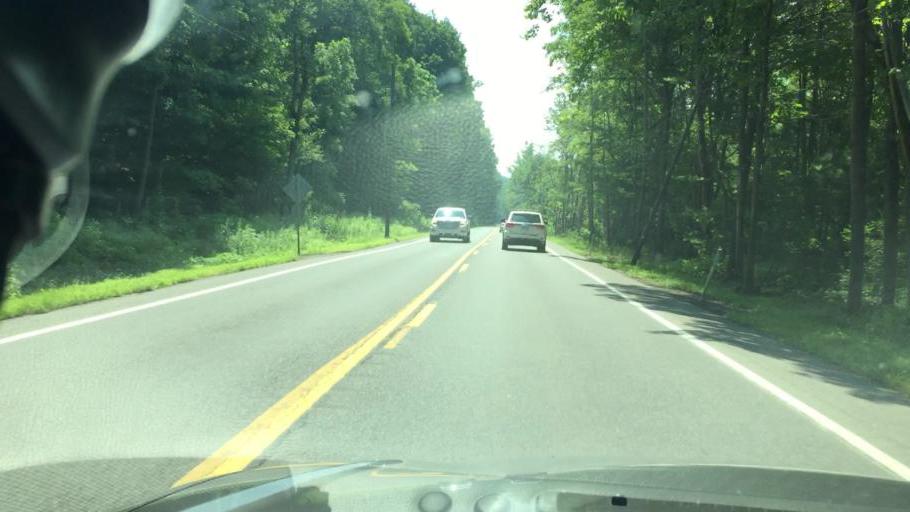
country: US
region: Pennsylvania
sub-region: Northumberland County
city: Elysburg
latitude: 40.8997
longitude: -76.5107
